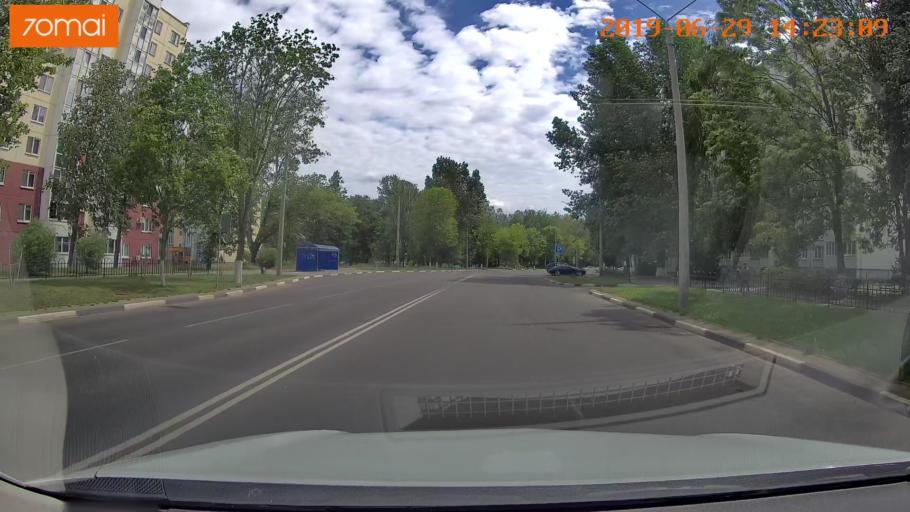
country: BY
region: Minsk
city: Salihorsk
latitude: 52.7876
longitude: 27.5536
